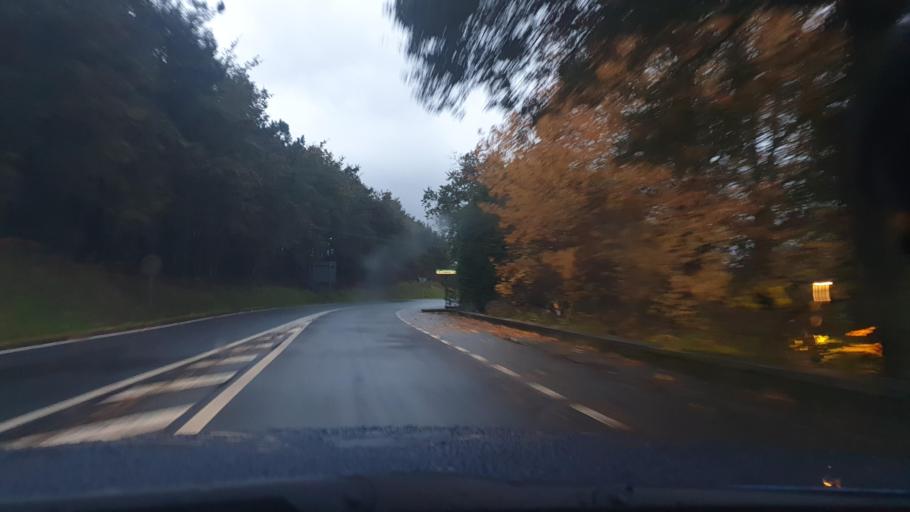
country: ES
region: Galicia
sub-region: Provincia da Coruna
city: Santiago de Compostela
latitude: 42.8420
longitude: -8.5963
